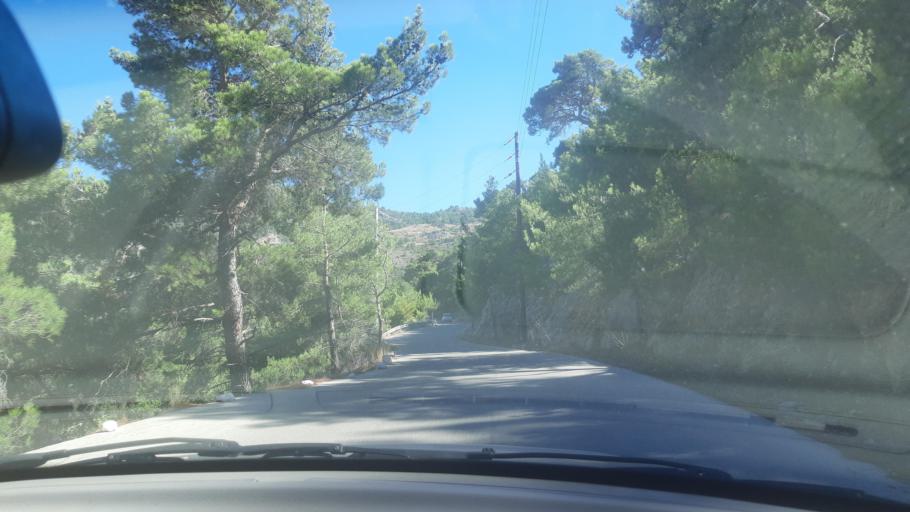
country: GR
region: South Aegean
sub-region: Nomos Dodekanisou
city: Karpathos
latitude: 35.5823
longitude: 27.1791
